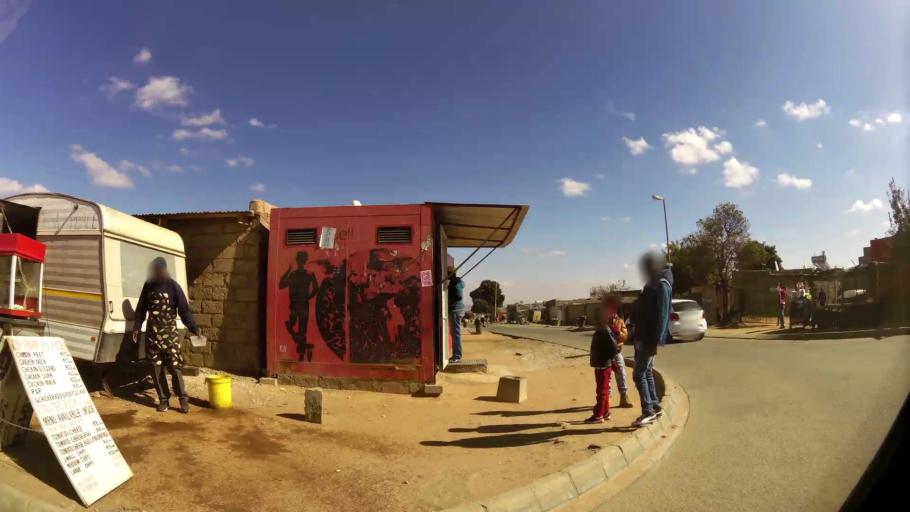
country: ZA
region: Gauteng
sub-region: City of Johannesburg Metropolitan Municipality
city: Modderfontein
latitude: -26.0322
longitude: 28.1692
